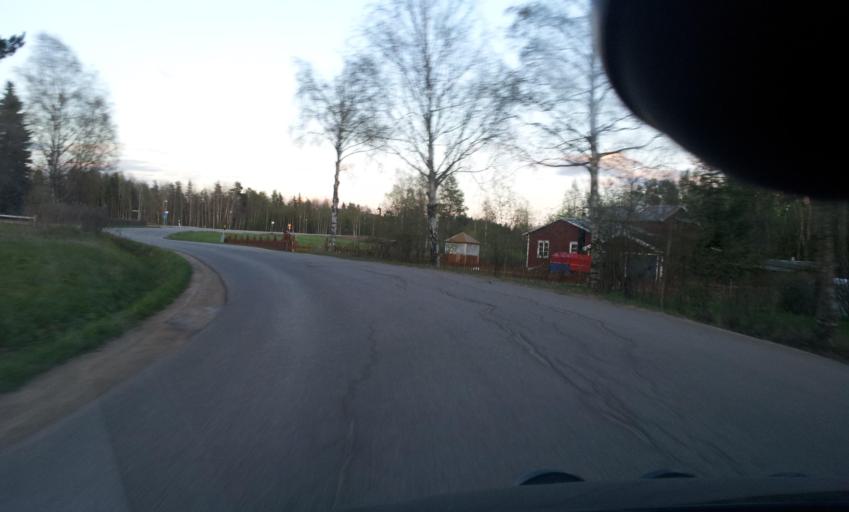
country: SE
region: Gaevleborg
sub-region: Bollnas Kommun
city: Bollnas
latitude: 61.3709
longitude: 16.3996
